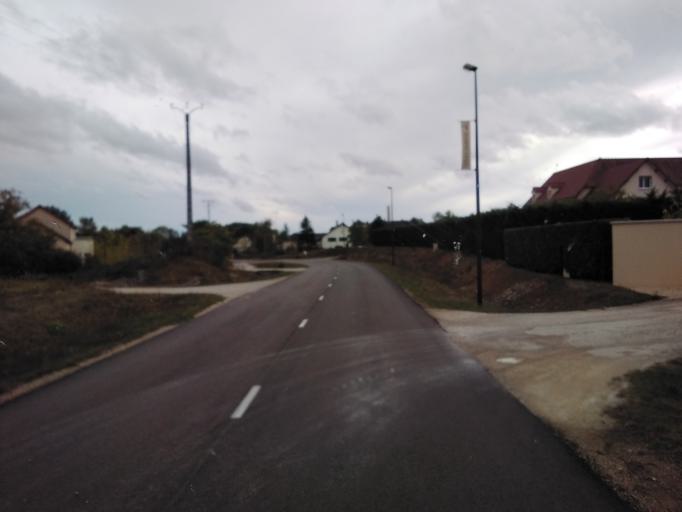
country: FR
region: Champagne-Ardenne
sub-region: Departement de l'Aube
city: Les Riceys
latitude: 47.9826
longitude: 4.3590
